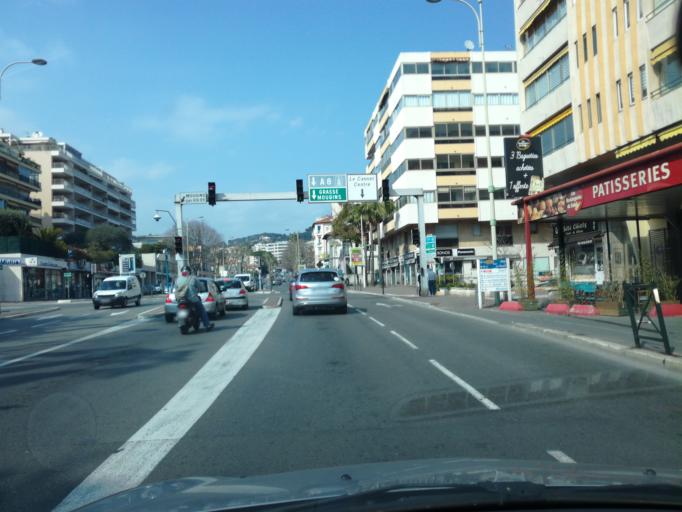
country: FR
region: Provence-Alpes-Cote d'Azur
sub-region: Departement des Alpes-Maritimes
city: Le Cannet
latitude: 43.5673
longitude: 7.0166
